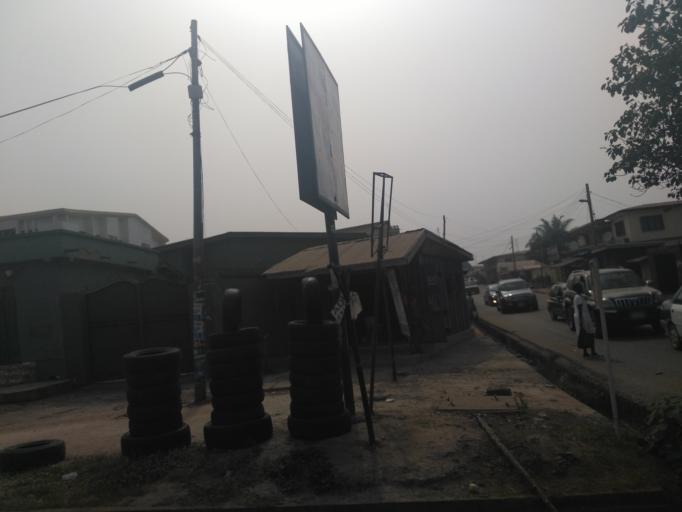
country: GH
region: Ashanti
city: Kumasi
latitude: 6.7104
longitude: -1.6385
